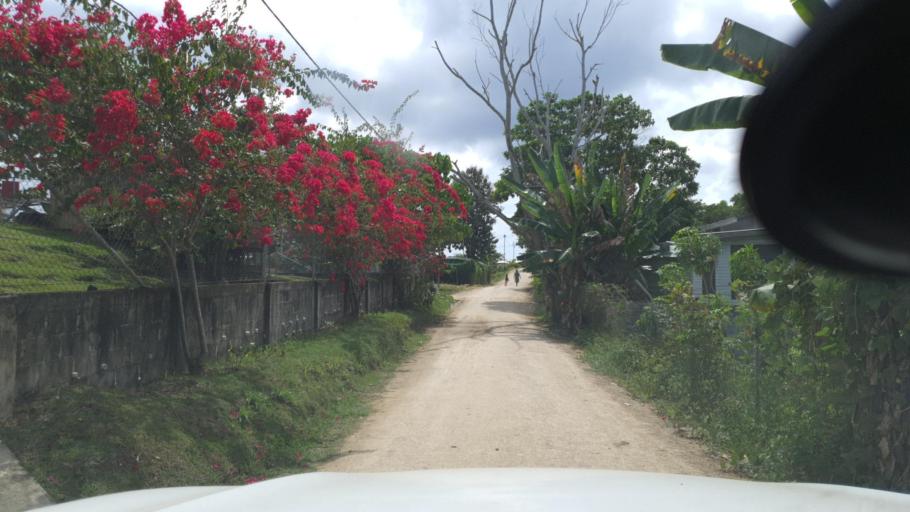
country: SB
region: Guadalcanal
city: Honiara
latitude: -9.4292
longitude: 159.9299
